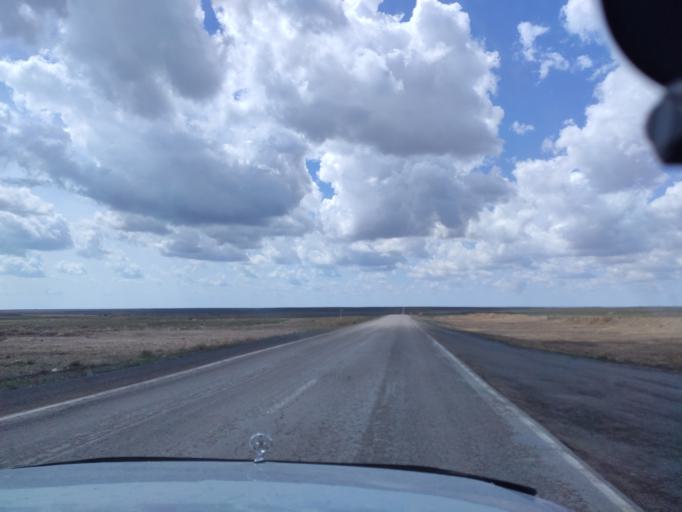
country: KZ
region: Qaraghandy
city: Saryshaghan
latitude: 46.0062
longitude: 73.5850
